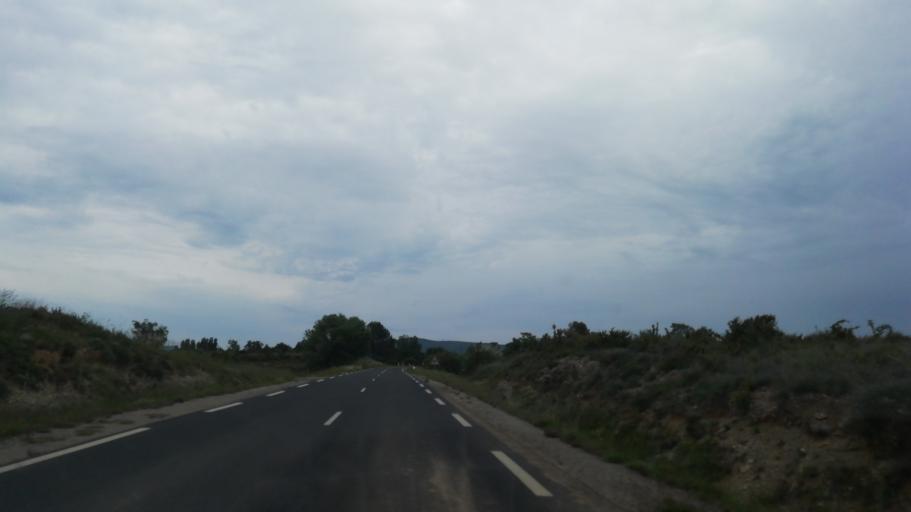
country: FR
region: Languedoc-Roussillon
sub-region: Departement de l'Herault
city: Saint-Martin-de-Londres
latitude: 43.7948
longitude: 3.7741
